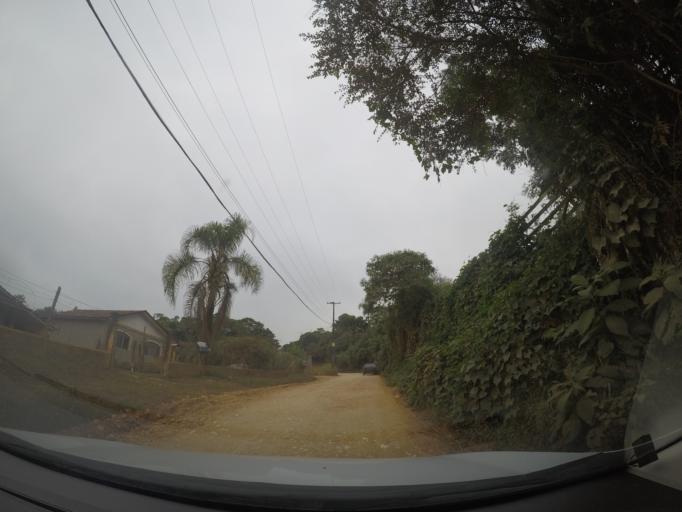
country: BR
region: Parana
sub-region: Colombo
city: Colombo
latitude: -25.3252
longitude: -49.2529
